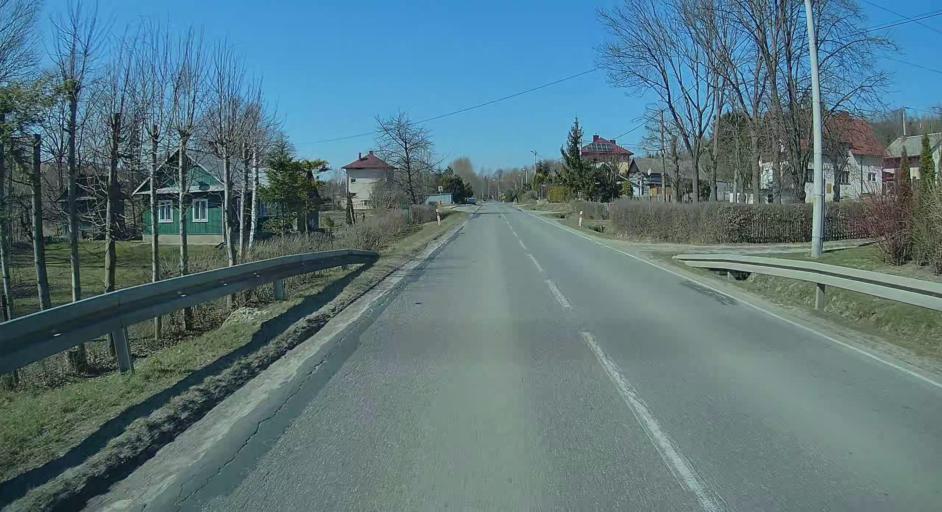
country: PL
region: Subcarpathian Voivodeship
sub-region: Powiat rzeszowski
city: Hyzne
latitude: 49.9131
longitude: 22.1943
